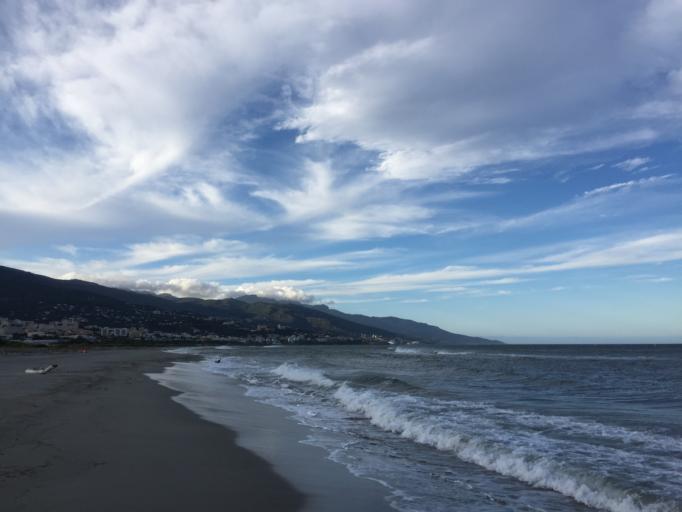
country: FR
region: Corsica
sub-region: Departement de la Haute-Corse
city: Biguglia
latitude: 42.6545
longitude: 9.4532
